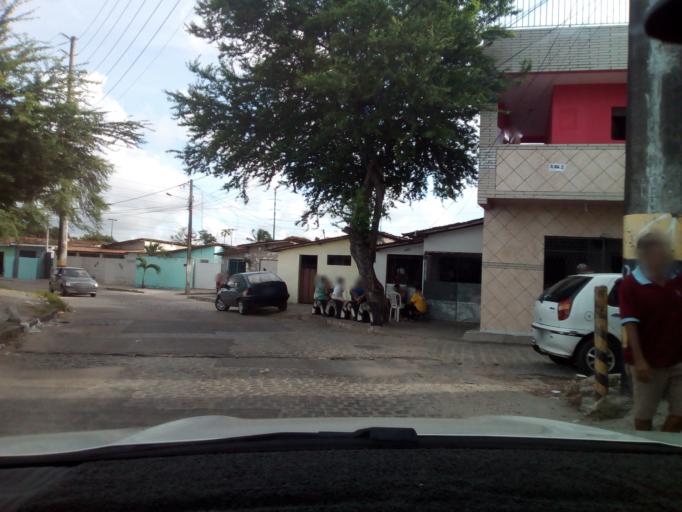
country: BR
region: Paraiba
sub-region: Joao Pessoa
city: Joao Pessoa
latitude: -7.1679
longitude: -34.8827
